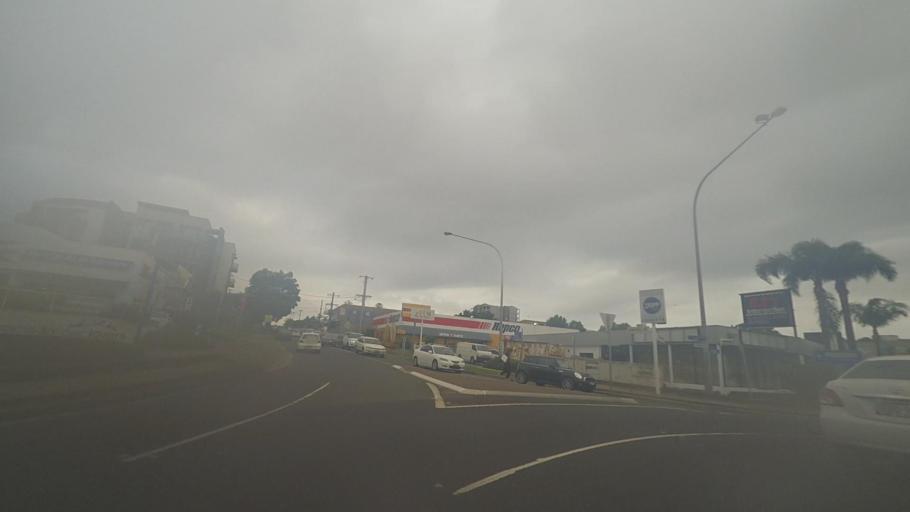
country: AU
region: New South Wales
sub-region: Wollongong
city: Wollongong
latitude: -34.4194
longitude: 150.8926
